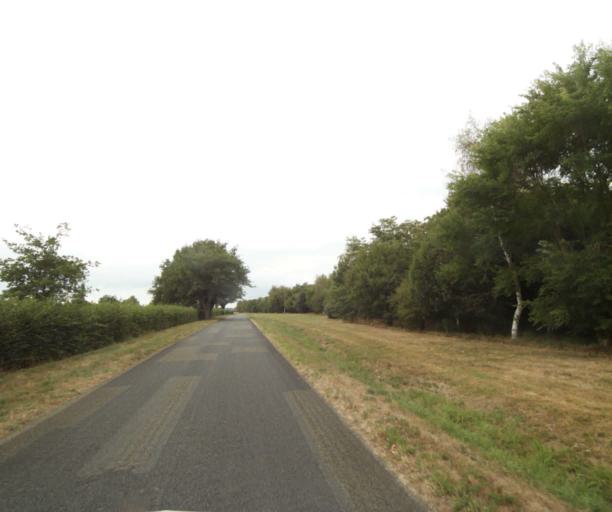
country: FR
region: Pays de la Loire
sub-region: Departement de la Sarthe
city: Sable-sur-Sarthe
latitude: 47.8155
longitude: -0.3515
